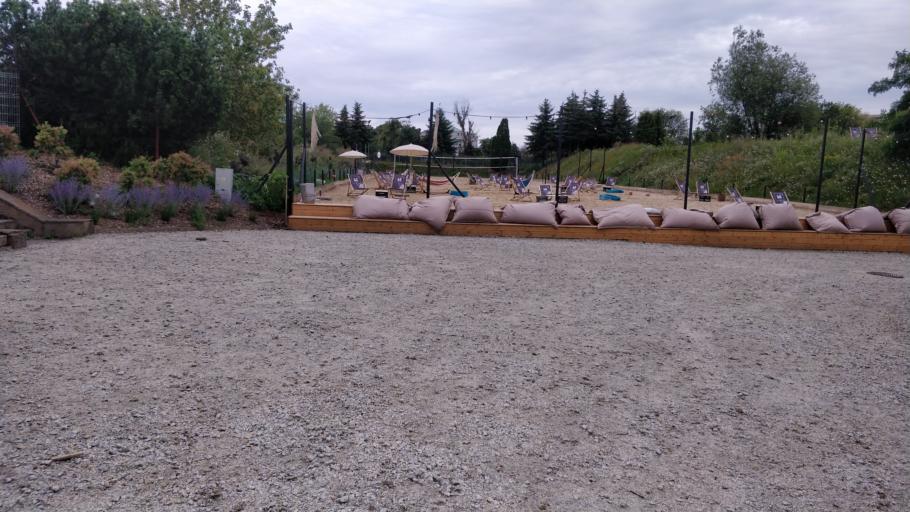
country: PL
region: Greater Poland Voivodeship
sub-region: Poznan
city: Poznan
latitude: 52.4263
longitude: 16.9439
